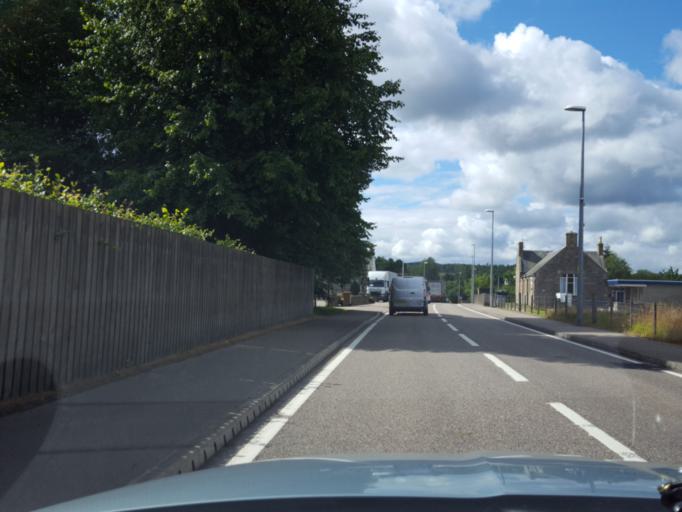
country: GB
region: Scotland
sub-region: Highland
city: Grantown on Spey
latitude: 57.3391
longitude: -3.5373
